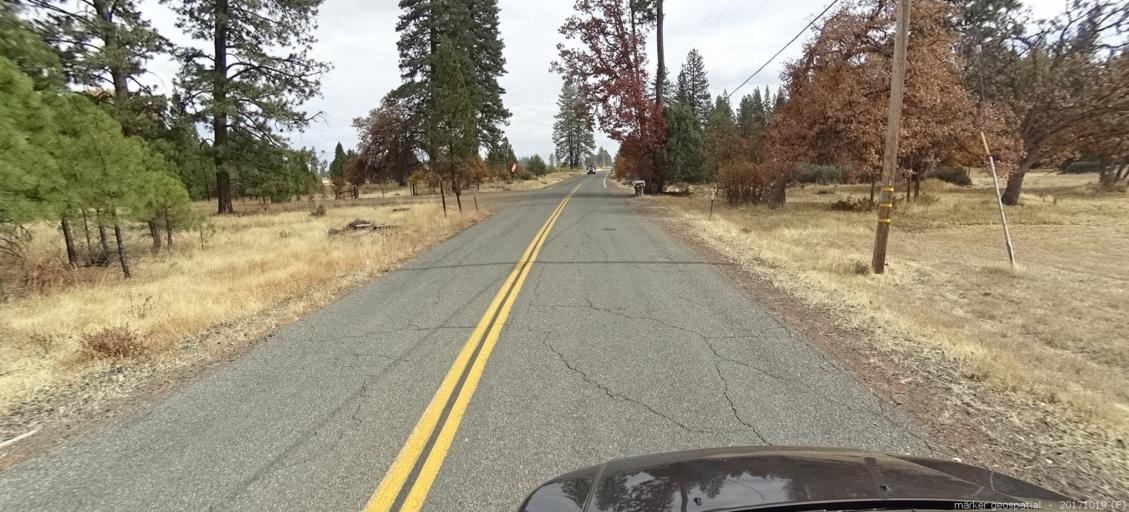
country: US
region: California
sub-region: Shasta County
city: Burney
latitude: 41.0618
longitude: -121.5357
